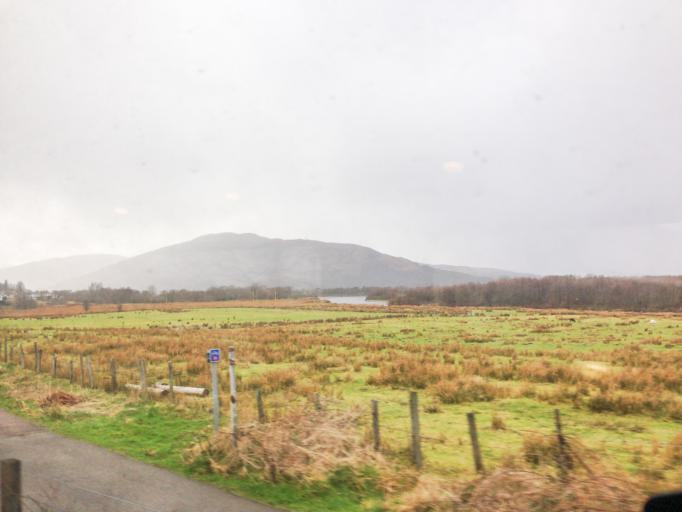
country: GB
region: Scotland
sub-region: Highland
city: Fort William
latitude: 56.8307
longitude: -5.0845
